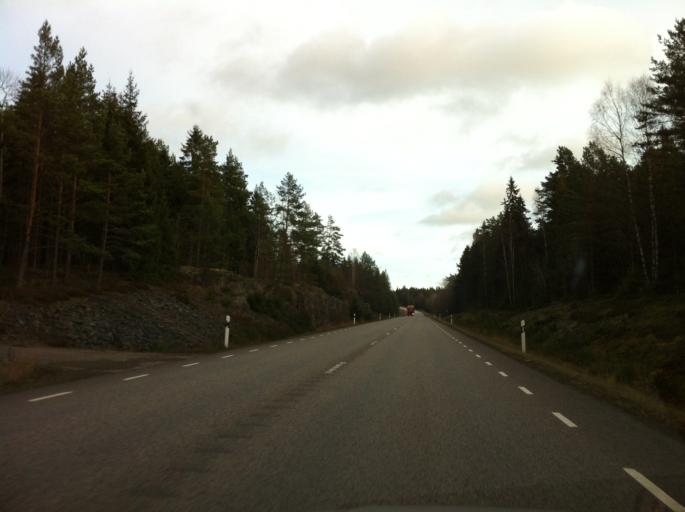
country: SE
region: Kronoberg
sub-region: Uppvidinge Kommun
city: Aseda
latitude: 57.1453
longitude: 15.2942
